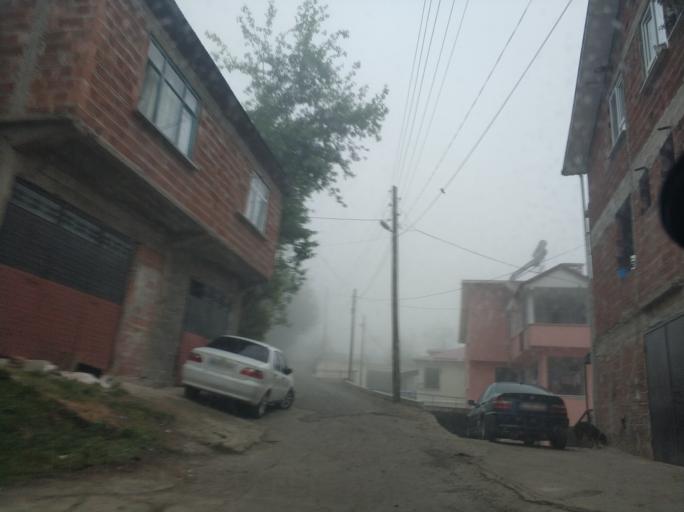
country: TR
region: Giresun
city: Nefsipiraziz
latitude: 40.8866
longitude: 38.0793
